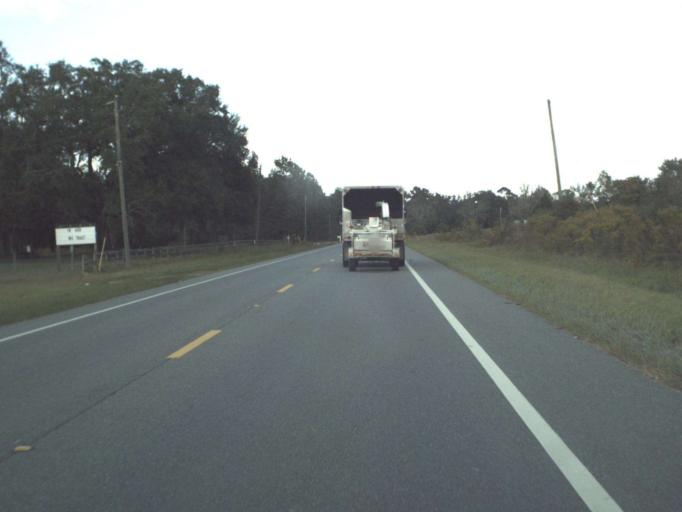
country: US
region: Florida
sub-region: Holmes County
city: Bonifay
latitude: 30.6768
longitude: -85.6386
